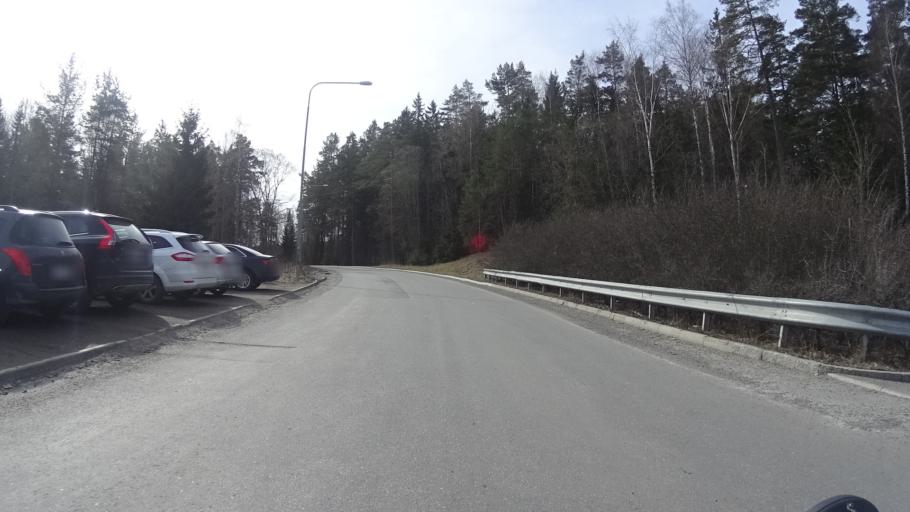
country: SE
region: Stockholm
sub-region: Taby Kommun
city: Taby
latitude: 59.4602
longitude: 18.1290
